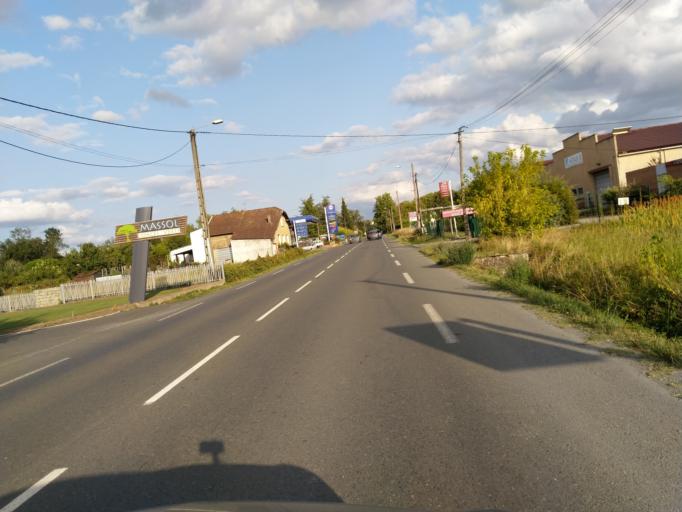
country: FR
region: Midi-Pyrenees
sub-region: Departement du Tarn
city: Puygouzon
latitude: 43.9196
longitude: 2.1754
